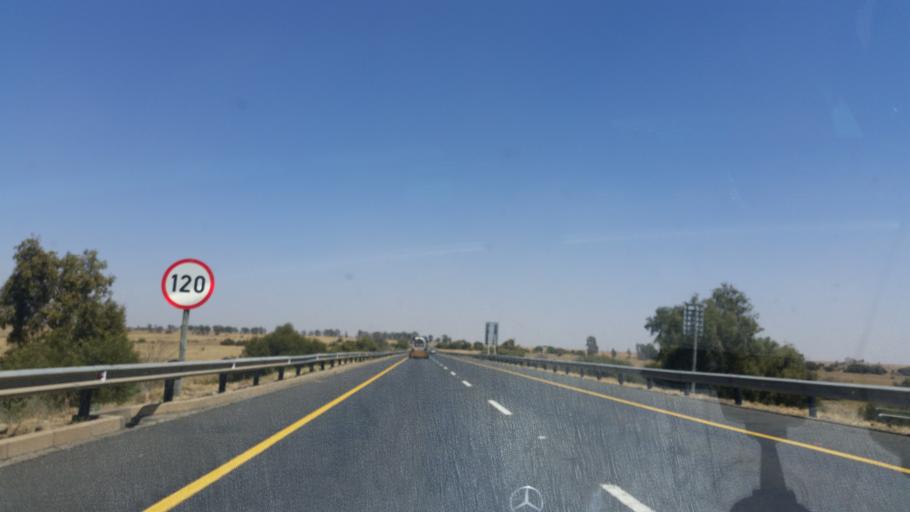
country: ZA
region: Orange Free State
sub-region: Lejweleputswa District Municipality
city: Winburg
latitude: -28.6324
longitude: 26.9025
